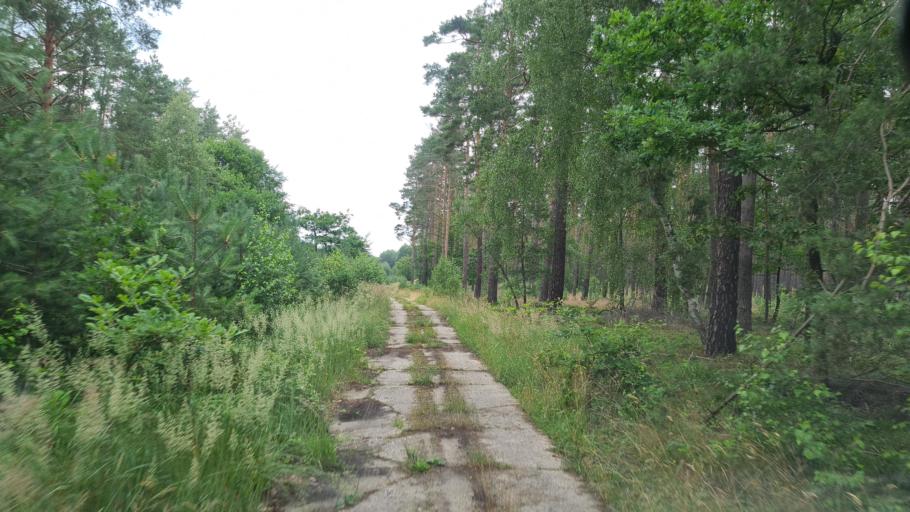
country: DE
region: Brandenburg
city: Crinitz
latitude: 51.7199
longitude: 13.7282
